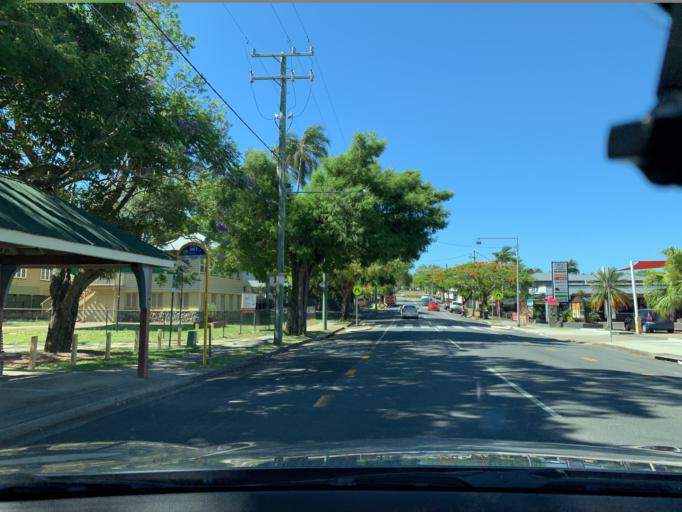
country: AU
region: Queensland
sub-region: Brisbane
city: Ascot
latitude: -27.4292
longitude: 153.0582
